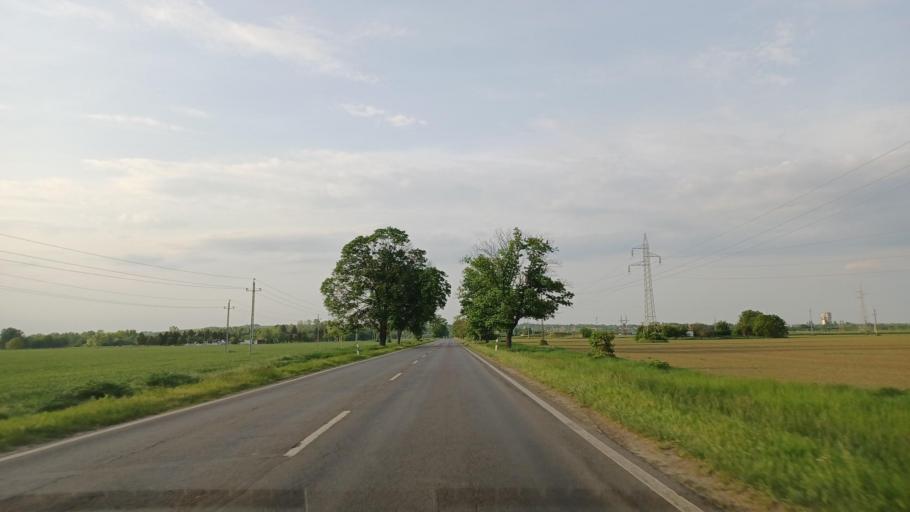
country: HU
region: Baranya
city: Lanycsok
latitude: 46.0086
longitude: 18.6549
